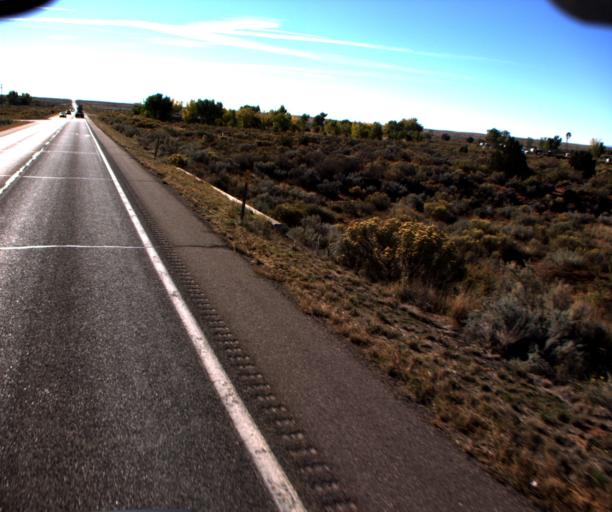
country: US
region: Arizona
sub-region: Mohave County
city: Colorado City
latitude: 36.9333
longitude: -112.9455
